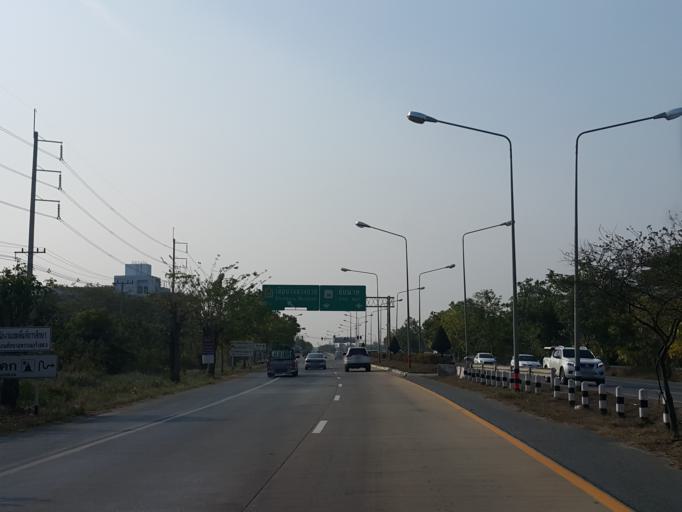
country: TH
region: Suphan Buri
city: Doem Bang Nang Buat
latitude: 14.8464
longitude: 100.1011
